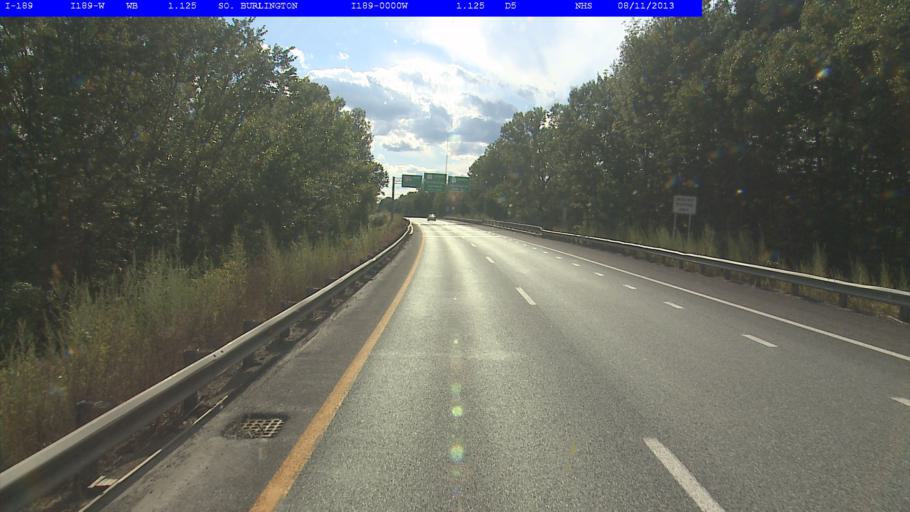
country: US
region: Vermont
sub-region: Chittenden County
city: South Burlington
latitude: 44.4519
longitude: -73.1878
